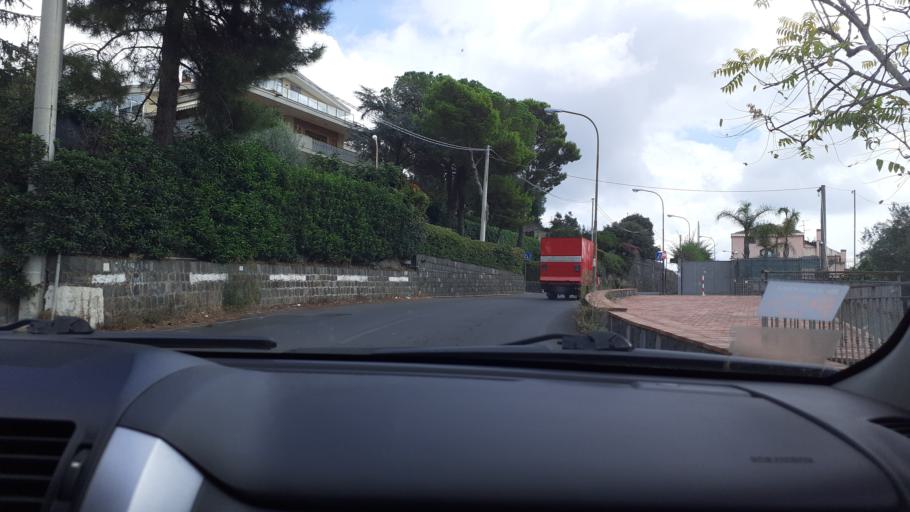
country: IT
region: Sicily
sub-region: Catania
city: Carrubazza-Motta
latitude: 37.5516
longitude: 15.1029
